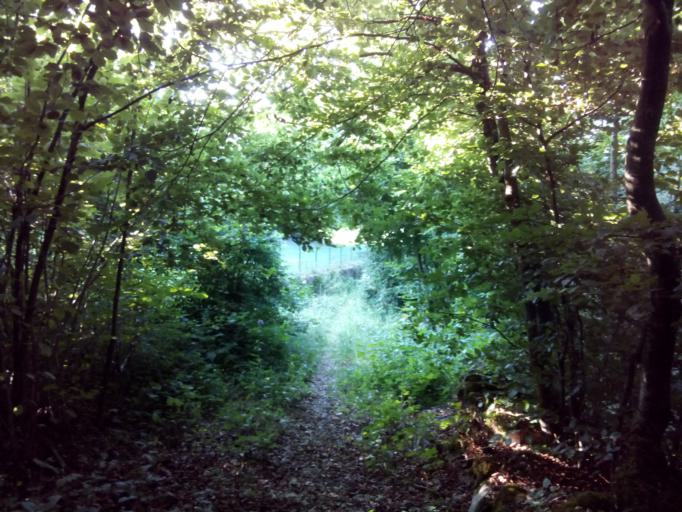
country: IT
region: Veneto
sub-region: Provincia di Vicenza
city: Conco
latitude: 45.8115
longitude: 11.6116
